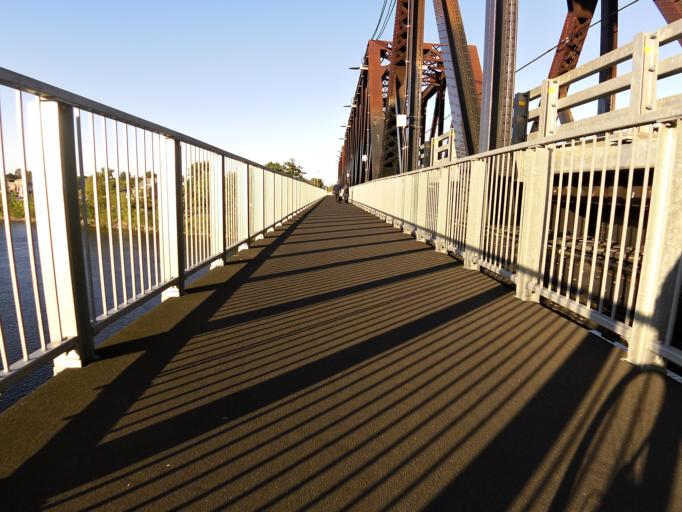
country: CA
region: Quebec
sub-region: Outaouais
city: Gatineau
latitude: 45.4632
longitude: -75.7252
